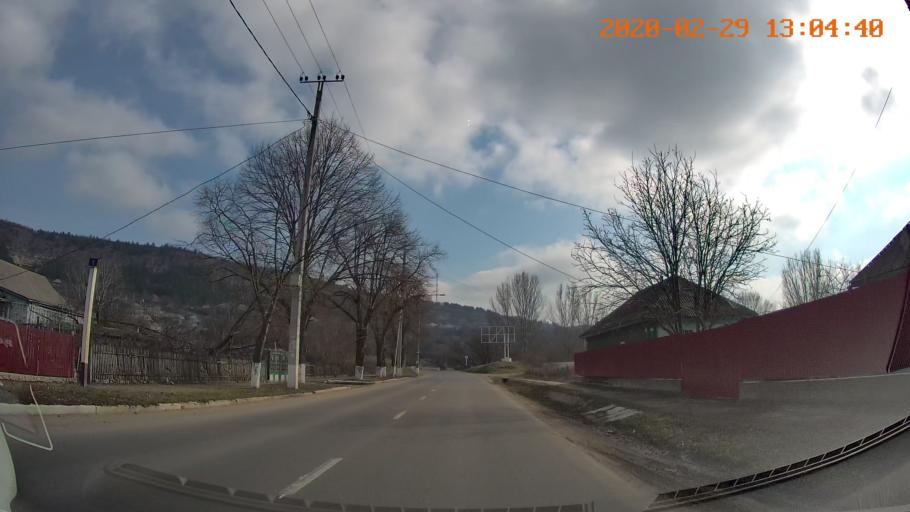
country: MD
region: Telenesti
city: Camenca
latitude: 48.0253
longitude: 28.7059
